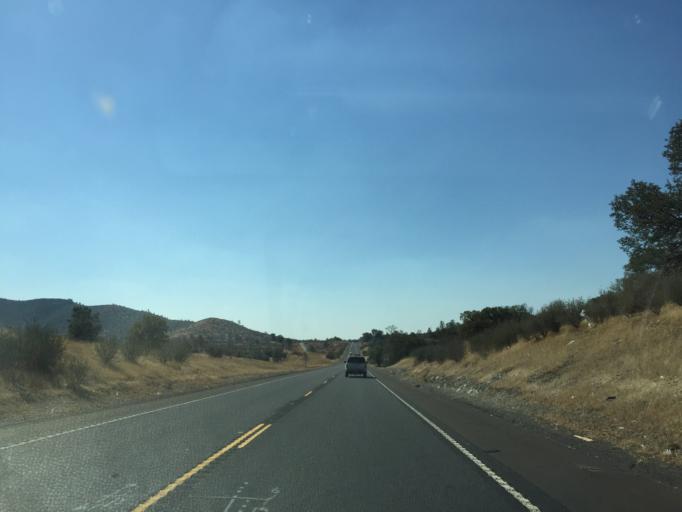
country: US
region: California
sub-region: Tuolumne County
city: Jamestown
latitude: 37.8786
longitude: -120.5068
